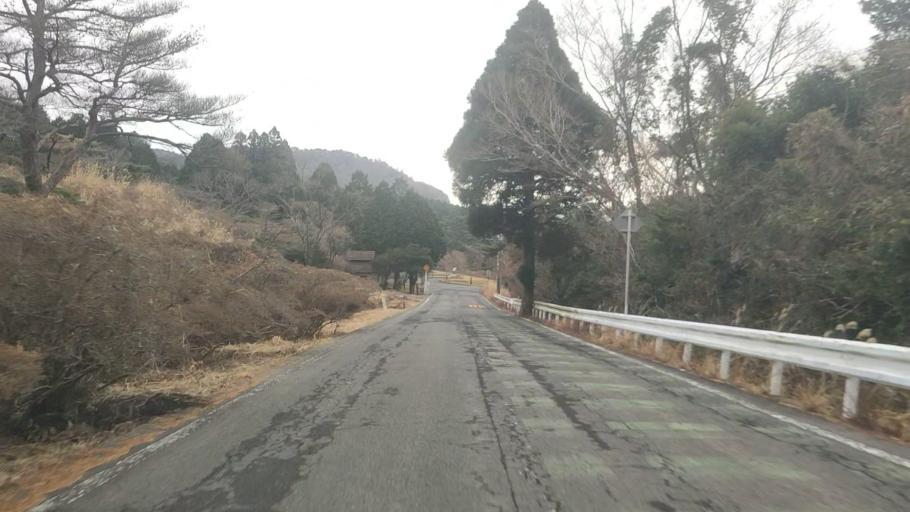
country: JP
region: Nagasaki
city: Shimabara
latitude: 32.7499
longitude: 130.2740
